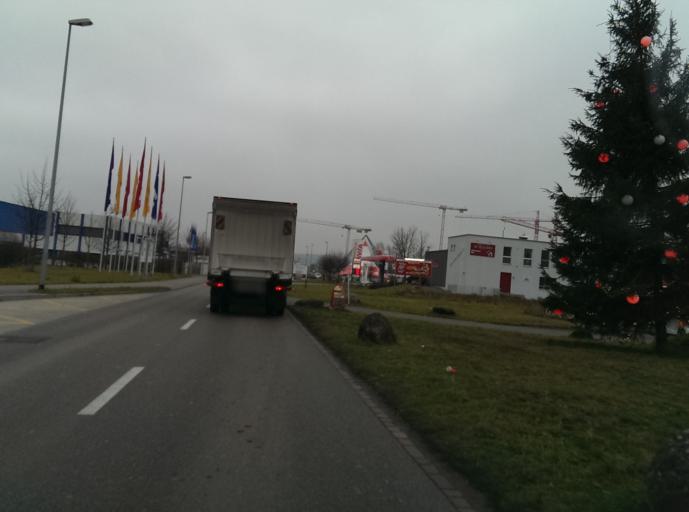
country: CH
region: Aargau
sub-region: Bezirk Baden
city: Spreitenbach
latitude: 47.4204
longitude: 8.3750
